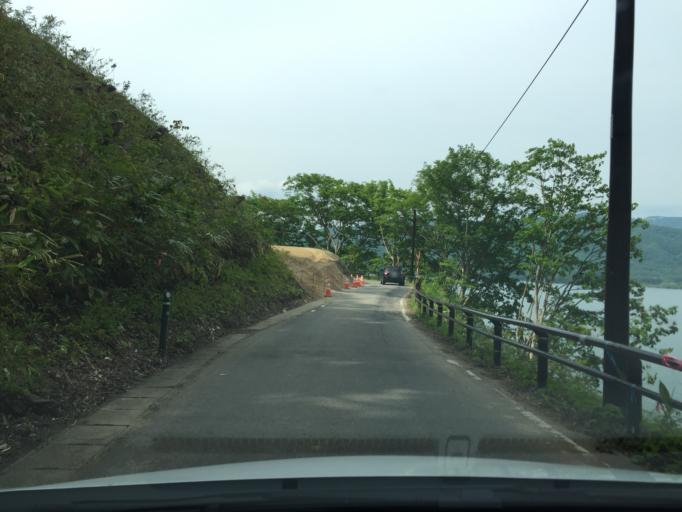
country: JP
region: Fukushima
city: Inawashiro
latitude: 37.7138
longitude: 140.0413
